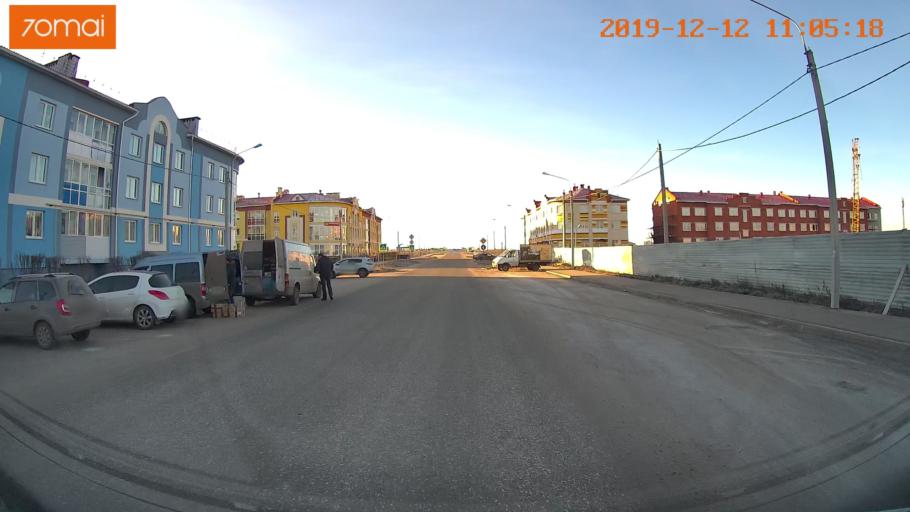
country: RU
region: Ivanovo
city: Kokhma
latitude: 56.9498
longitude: 41.1000
